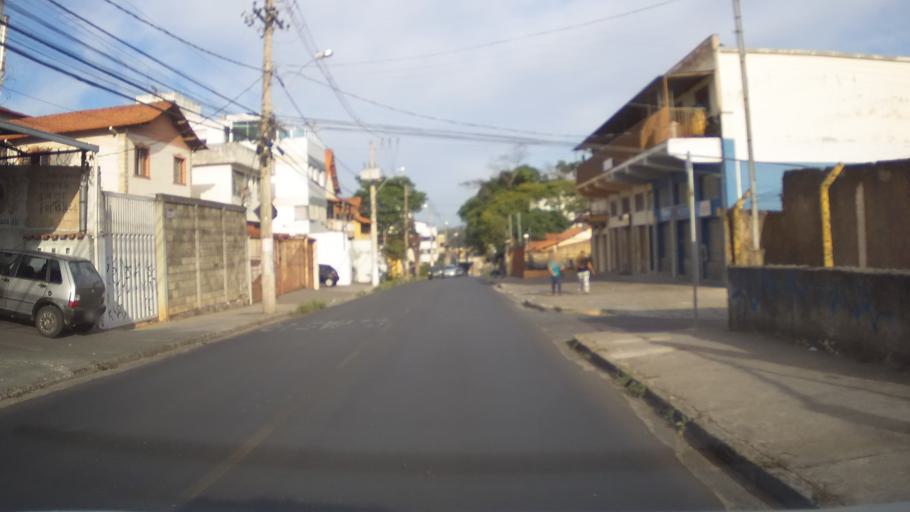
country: BR
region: Minas Gerais
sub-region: Belo Horizonte
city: Belo Horizonte
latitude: -19.8697
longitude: -43.9946
